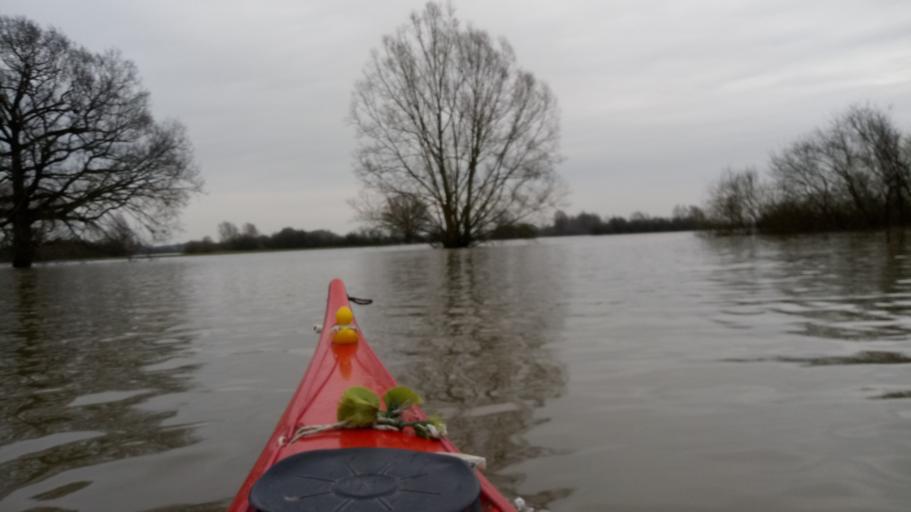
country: NL
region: Gelderland
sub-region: Gemeente Voorst
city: Voorst
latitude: 52.1823
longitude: 6.1688
